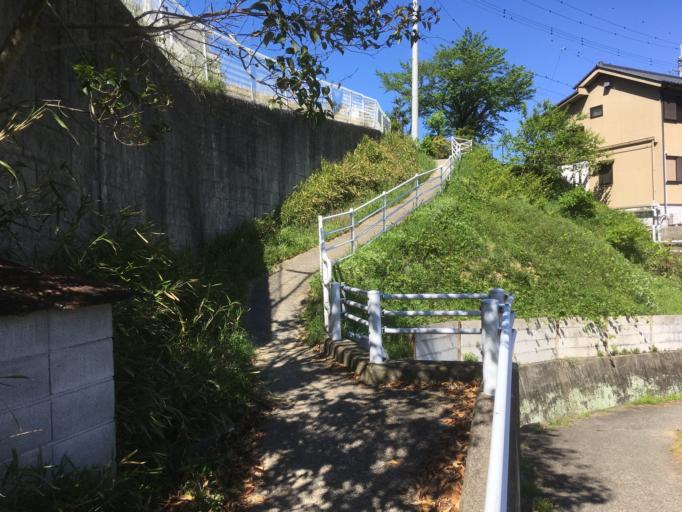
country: JP
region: Nara
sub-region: Ikoma-shi
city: Ikoma
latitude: 34.6879
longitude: 135.6973
